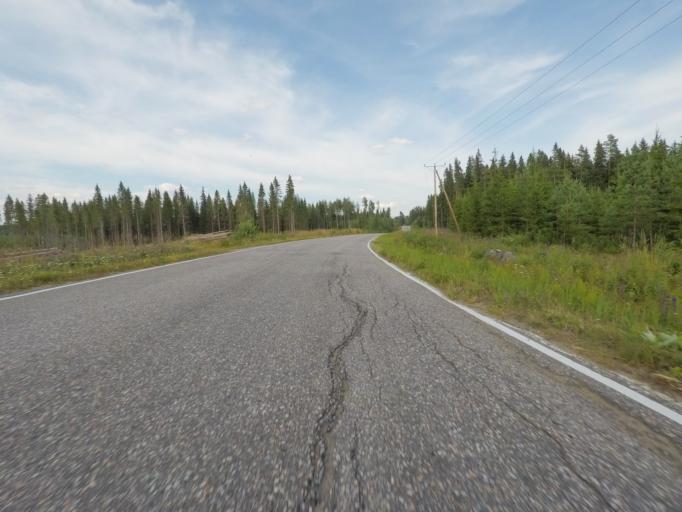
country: FI
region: Southern Savonia
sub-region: Savonlinna
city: Sulkava
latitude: 61.7481
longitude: 28.2020
